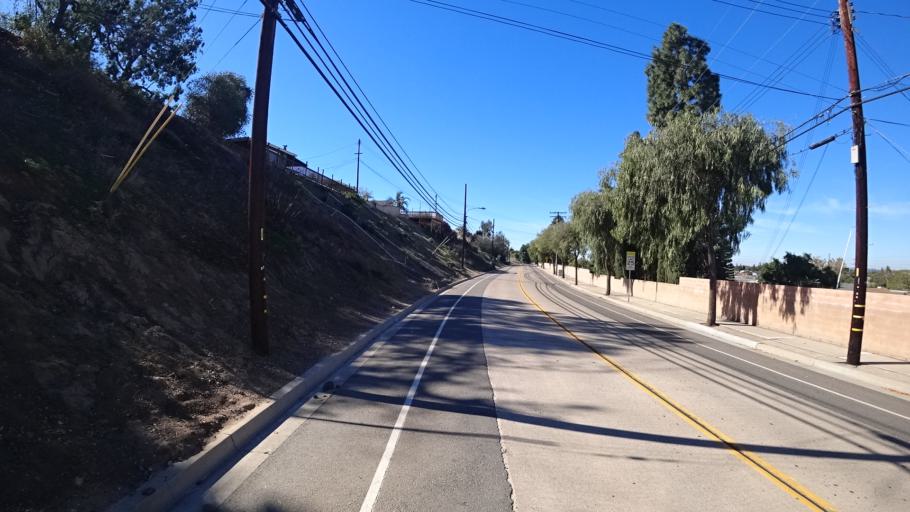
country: US
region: California
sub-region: Orange County
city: Villa Park
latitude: 33.8419
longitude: -117.8414
